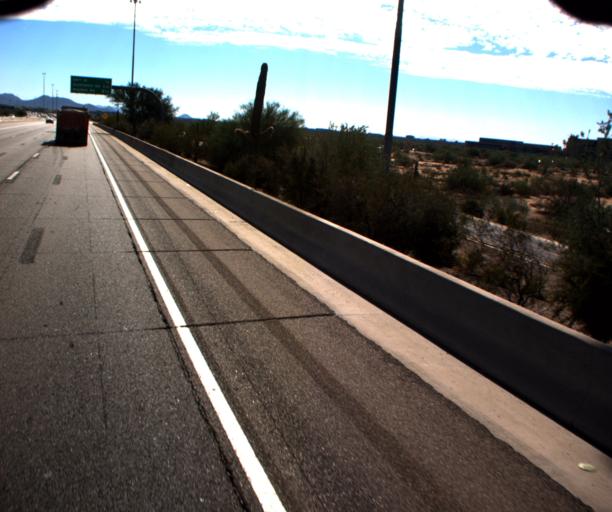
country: US
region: Arizona
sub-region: Maricopa County
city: Paradise Valley
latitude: 33.6672
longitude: -111.9589
